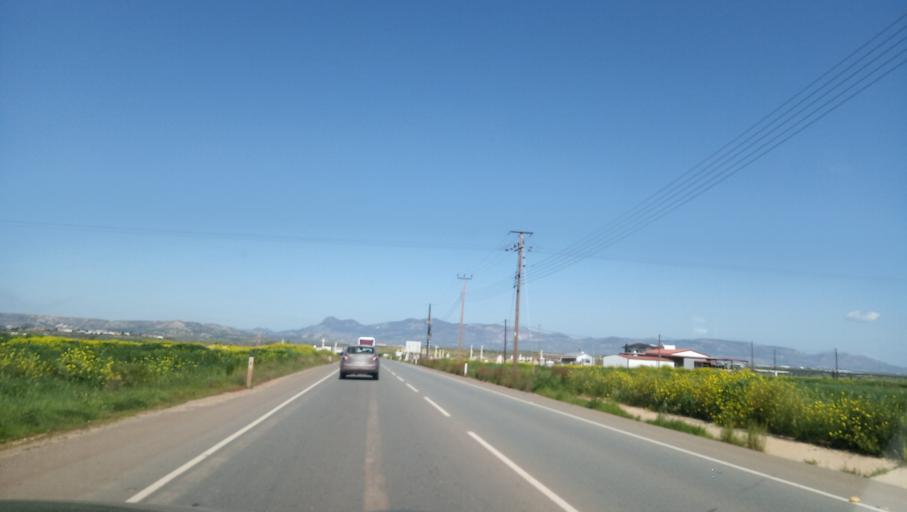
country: CY
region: Lefkosia
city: Akaki
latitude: 35.1451
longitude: 33.1559
